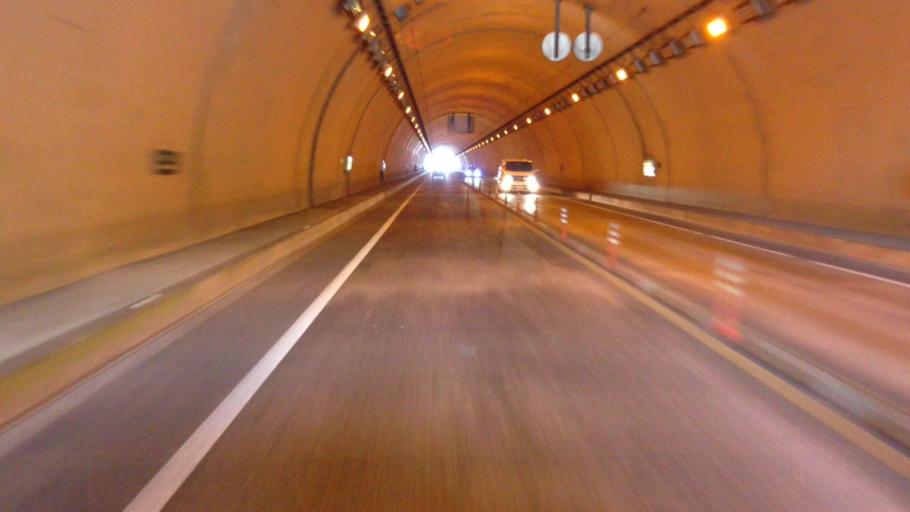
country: JP
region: Kanagawa
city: Yokosuka
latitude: 35.2412
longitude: 139.6540
